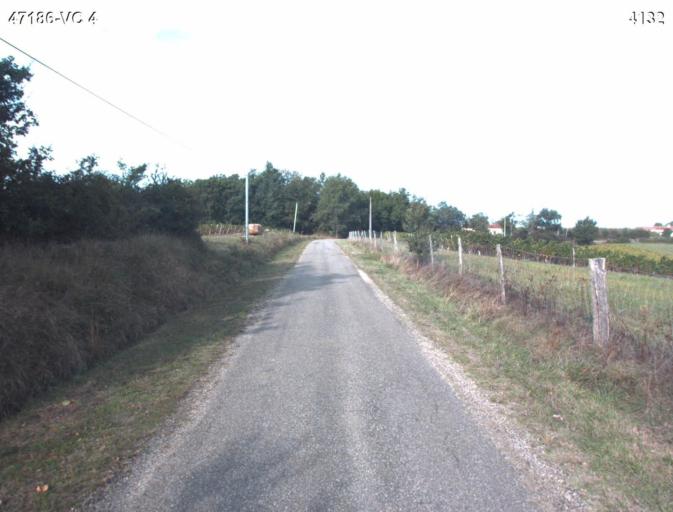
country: FR
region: Aquitaine
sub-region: Departement du Lot-et-Garonne
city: Sainte-Colombe-en-Bruilhois
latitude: 44.1956
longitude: 0.4486
